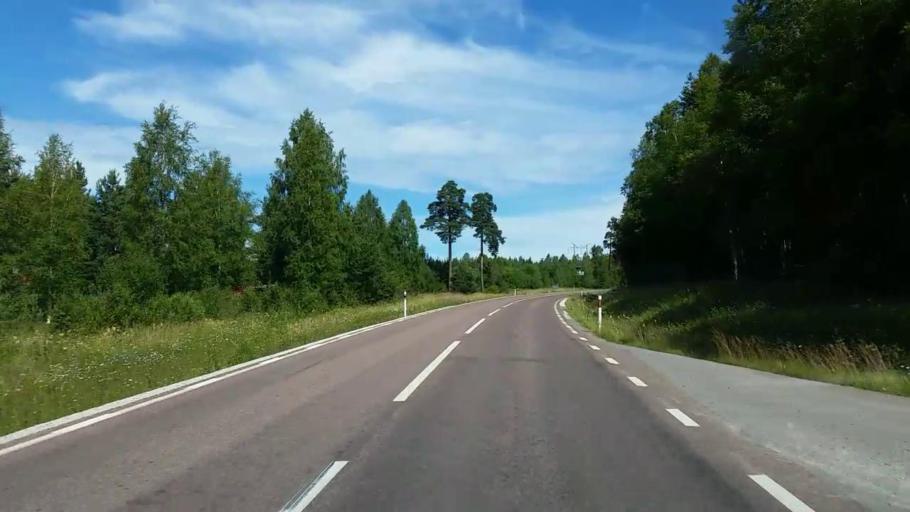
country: SE
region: Dalarna
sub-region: Rattviks Kommun
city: Raettvik
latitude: 60.8955
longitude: 15.1487
